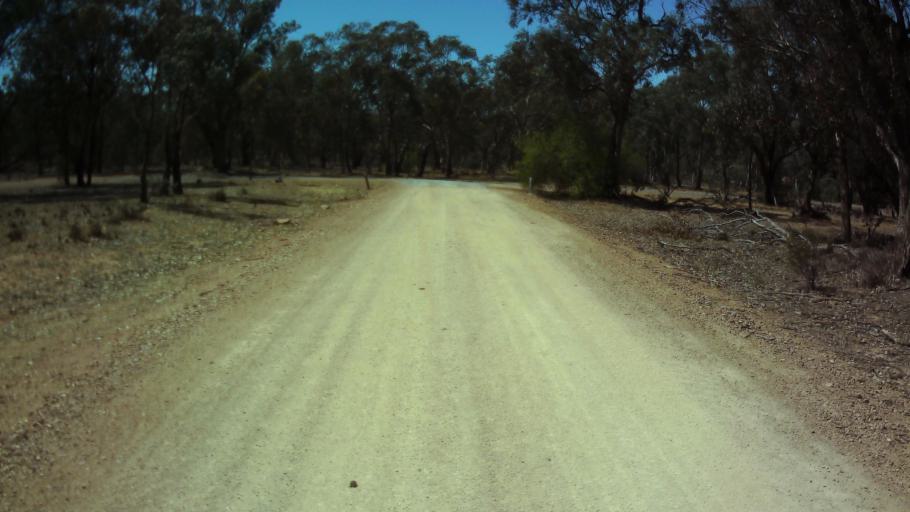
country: AU
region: New South Wales
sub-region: Weddin
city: Grenfell
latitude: -33.9390
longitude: 148.0785
